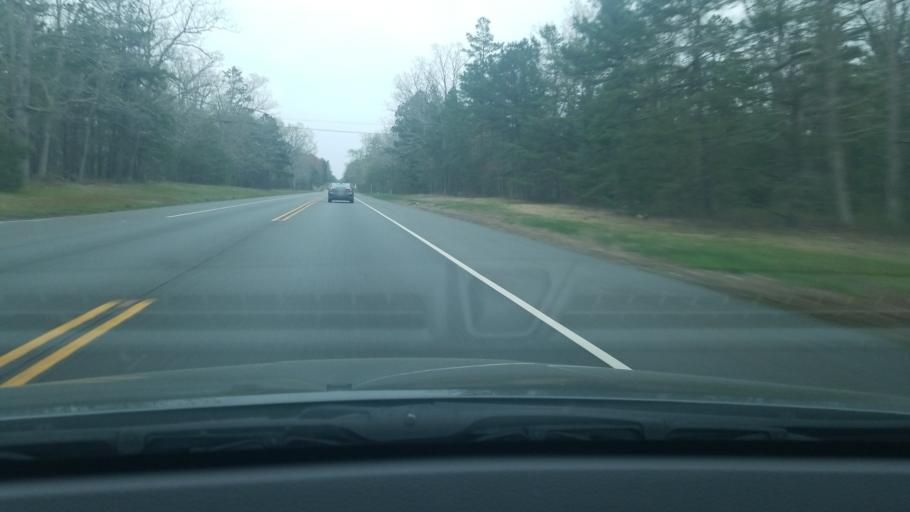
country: US
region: New Jersey
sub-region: Burlington County
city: Leisuretowne
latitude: 39.8890
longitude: -74.6524
